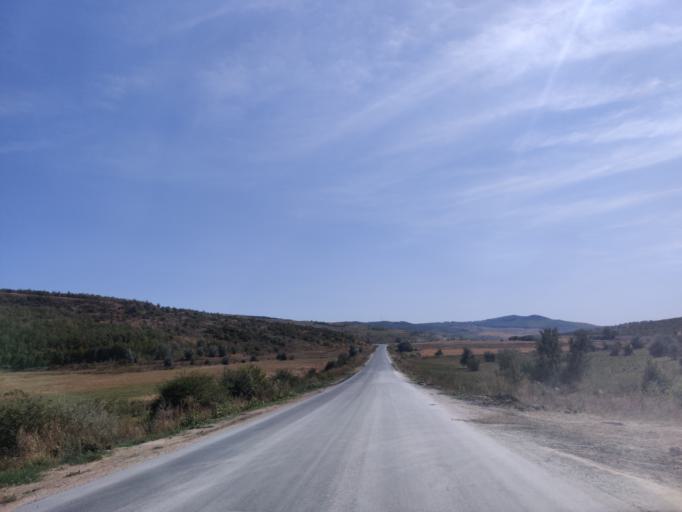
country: MD
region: Ungheni
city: Ungheni
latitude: 47.2525
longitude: 27.9978
